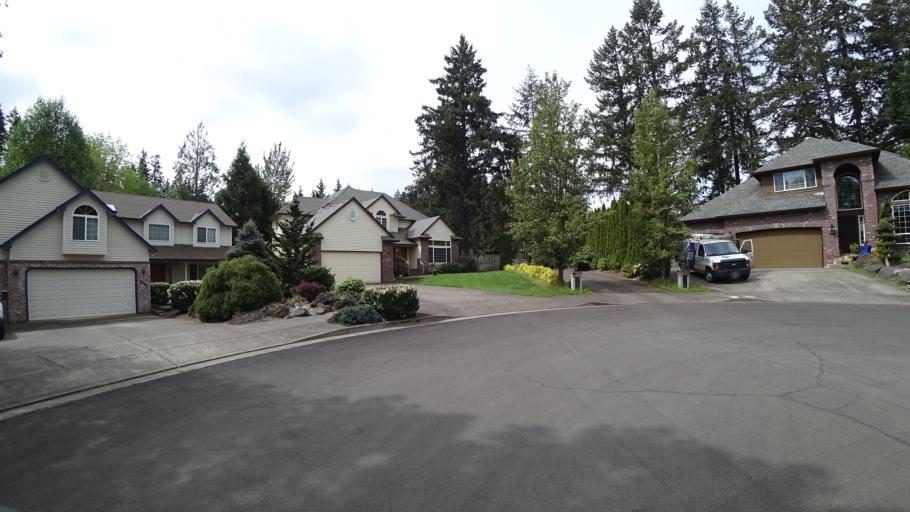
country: US
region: Oregon
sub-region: Washington County
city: Hillsboro
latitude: 45.5436
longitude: -122.9889
